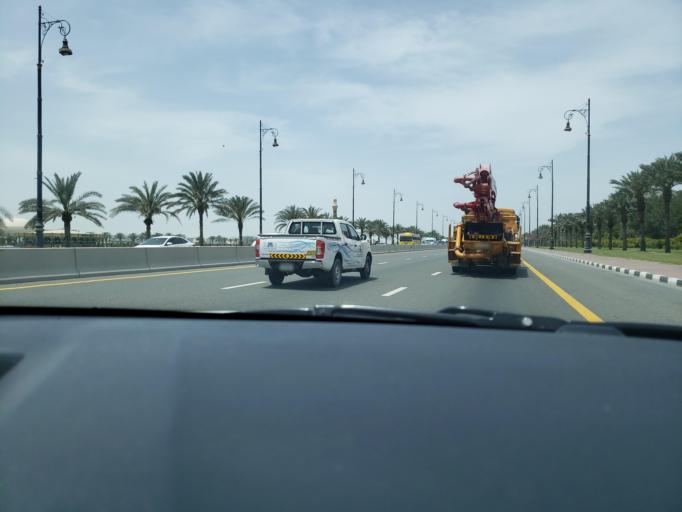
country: AE
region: Ash Shariqah
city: Sharjah
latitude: 25.3233
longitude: 55.4988
